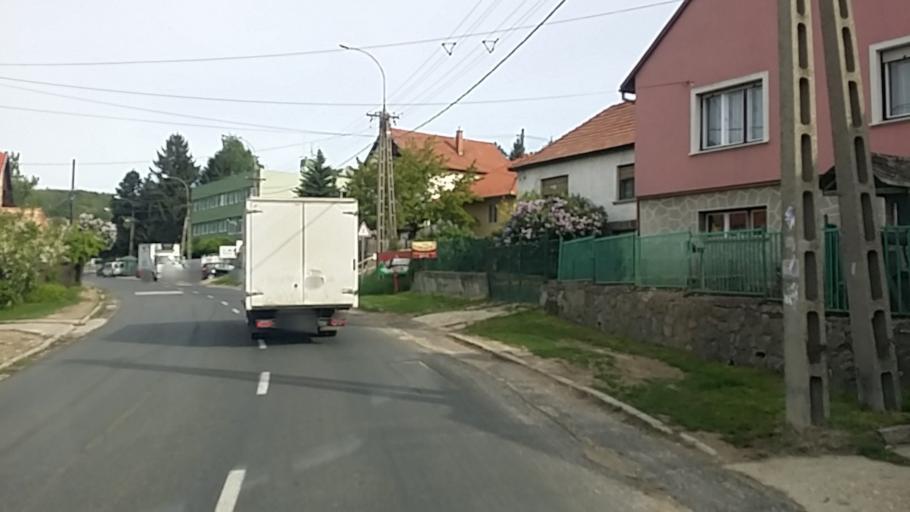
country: HU
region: Pest
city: Pilisszentkereszt
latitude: 47.6928
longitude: 18.9038
